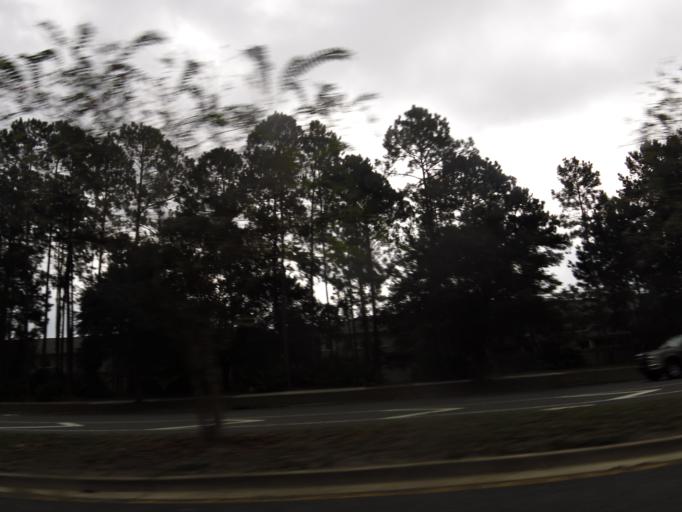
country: US
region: Florida
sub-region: Clay County
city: Lakeside
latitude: 30.1735
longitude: -81.8510
